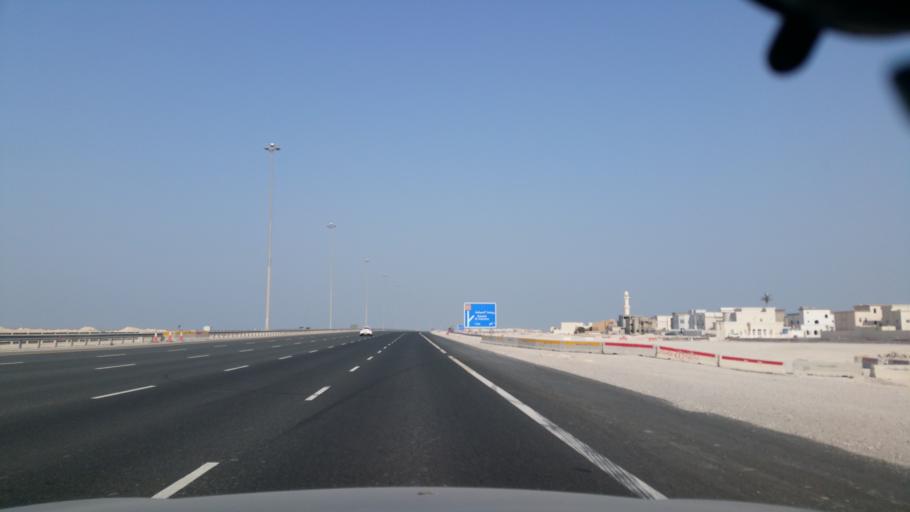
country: QA
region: Baladiyat Umm Salal
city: Umm Salal `Ali
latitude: 25.4547
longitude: 51.4349
